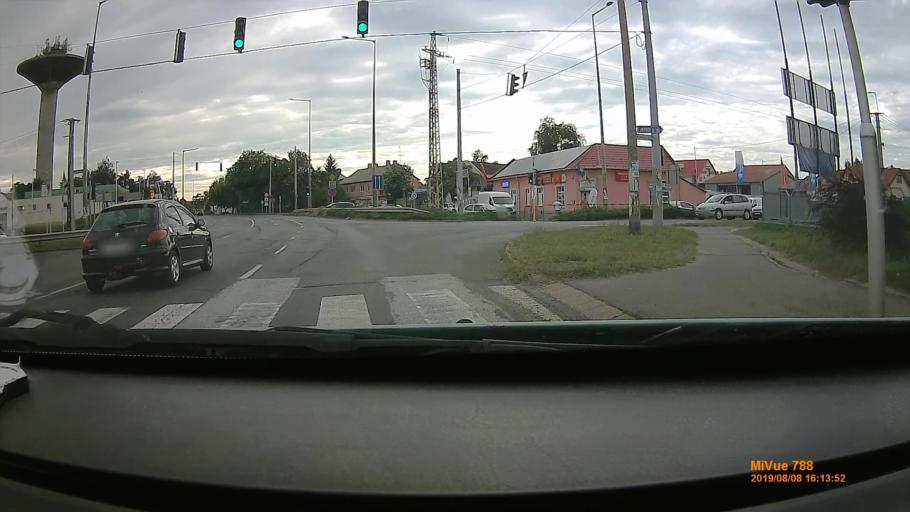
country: HU
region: Szabolcs-Szatmar-Bereg
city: Mateszalka
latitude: 47.9600
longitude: 22.3217
